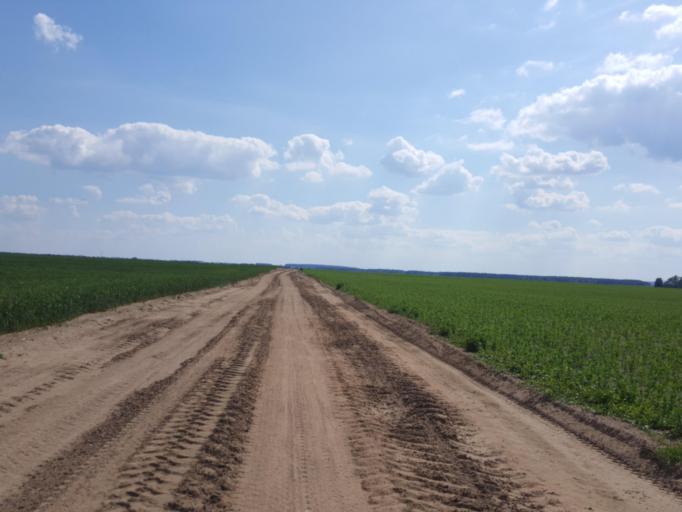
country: BY
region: Brest
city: Kamyanyuki
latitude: 52.4933
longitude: 23.6014
